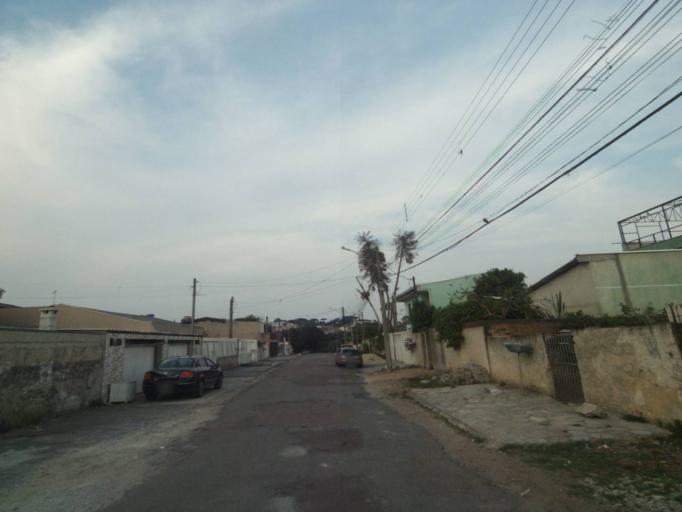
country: BR
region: Parana
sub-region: Sao Jose Dos Pinhais
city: Sao Jose dos Pinhais
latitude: -25.5231
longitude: -49.2687
